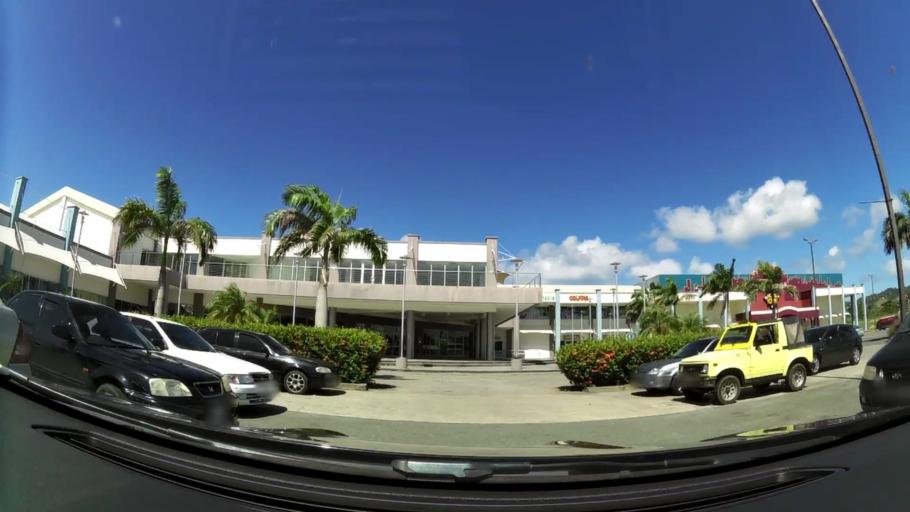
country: TT
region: Tobago
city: Scarborough
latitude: 11.1613
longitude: -60.7788
